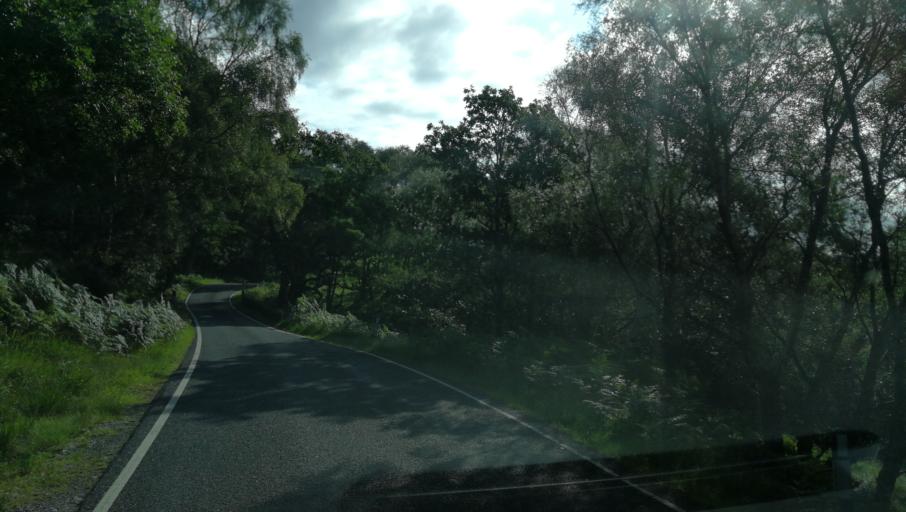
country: GB
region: Scotland
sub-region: Argyll and Bute
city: Isle Of Mull
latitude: 56.6785
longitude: -5.8414
